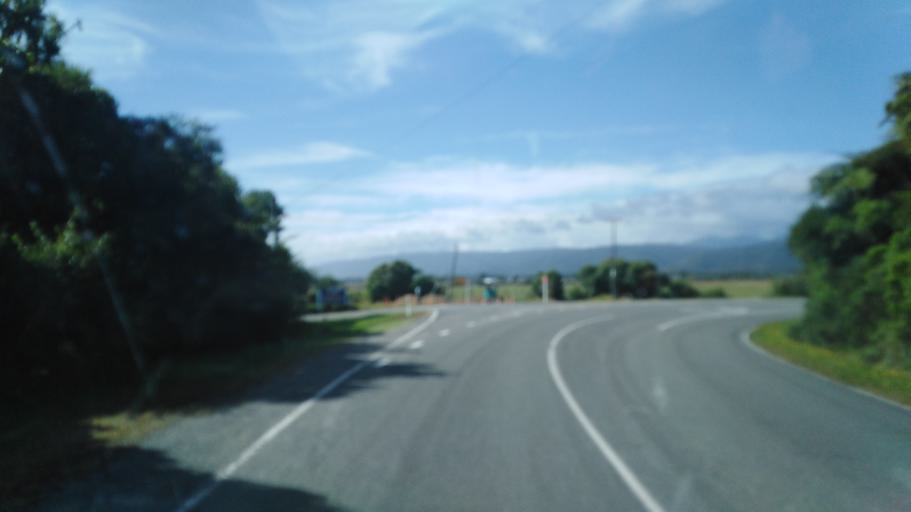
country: NZ
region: West Coast
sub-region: Buller District
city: Westport
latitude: -41.2571
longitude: 172.1131
